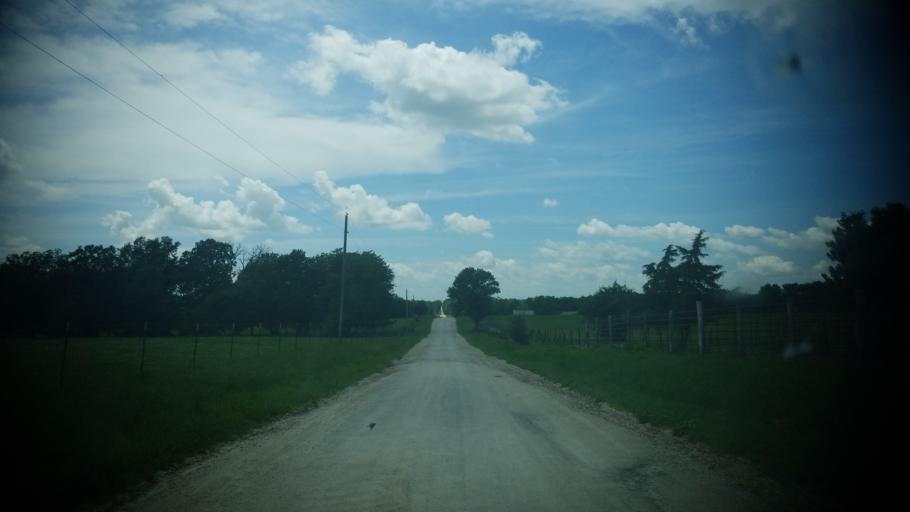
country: US
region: Missouri
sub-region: Pike County
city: Bowling Green
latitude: 39.3086
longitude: -91.3187
